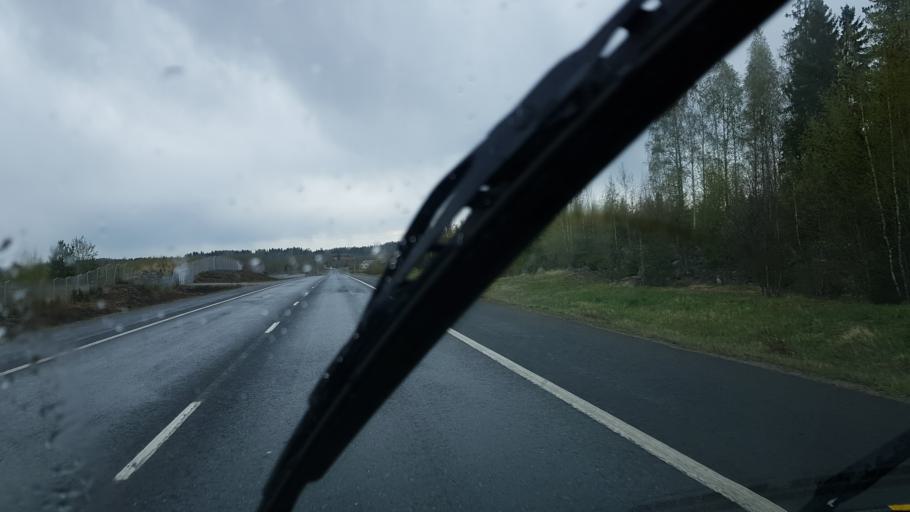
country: FI
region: Pirkanmaa
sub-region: Tampere
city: Pirkkala
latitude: 61.4162
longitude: 23.6343
